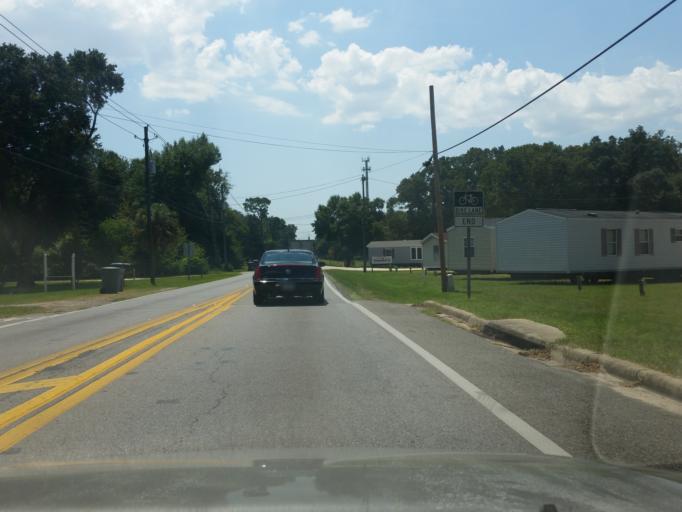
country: US
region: Florida
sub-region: Escambia County
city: Ensley
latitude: 30.5469
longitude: -87.2809
